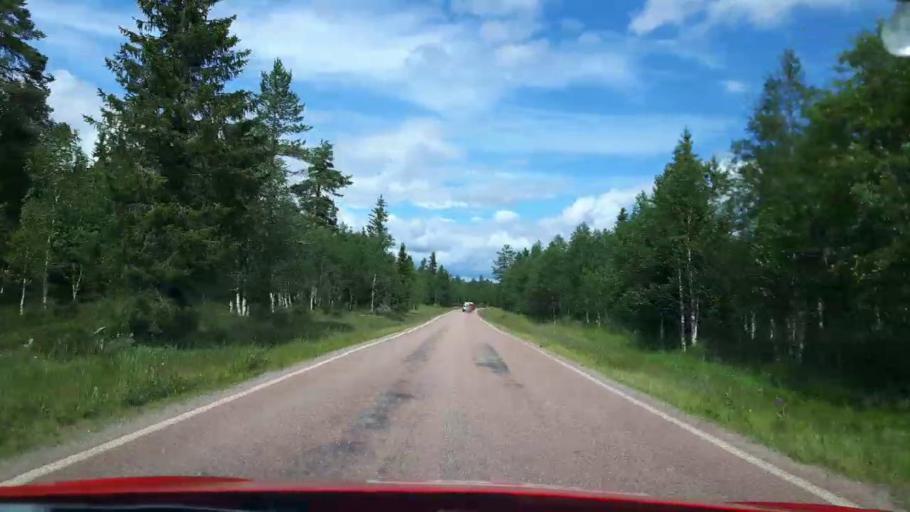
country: NO
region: Hedmark
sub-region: Trysil
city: Innbygda
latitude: 62.0075
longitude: 12.9754
